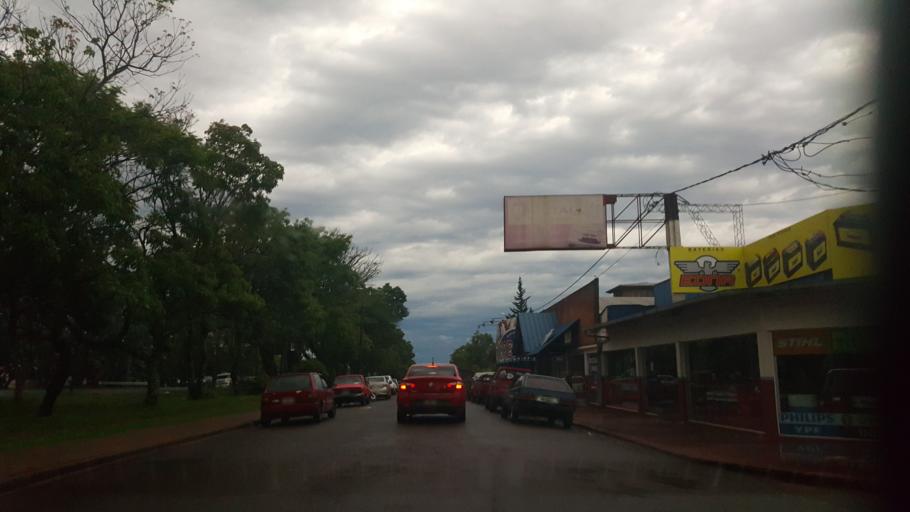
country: AR
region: Misiones
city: Jardin America
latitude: -27.0470
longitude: -55.2416
